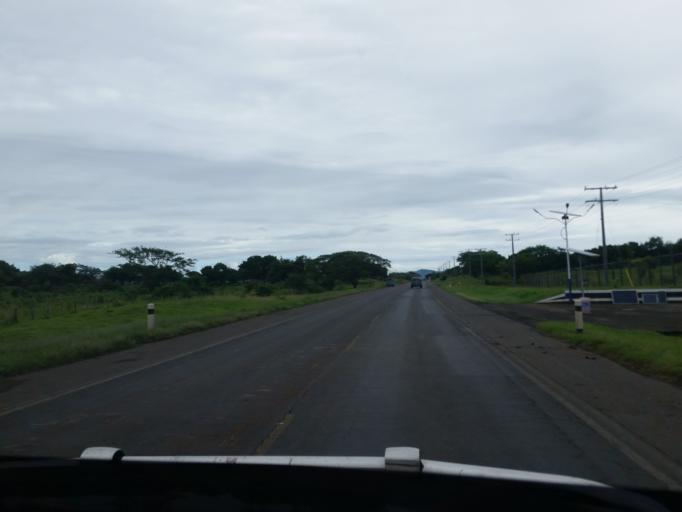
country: NI
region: Managua
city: Tipitapa
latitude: 12.2608
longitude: -86.0819
